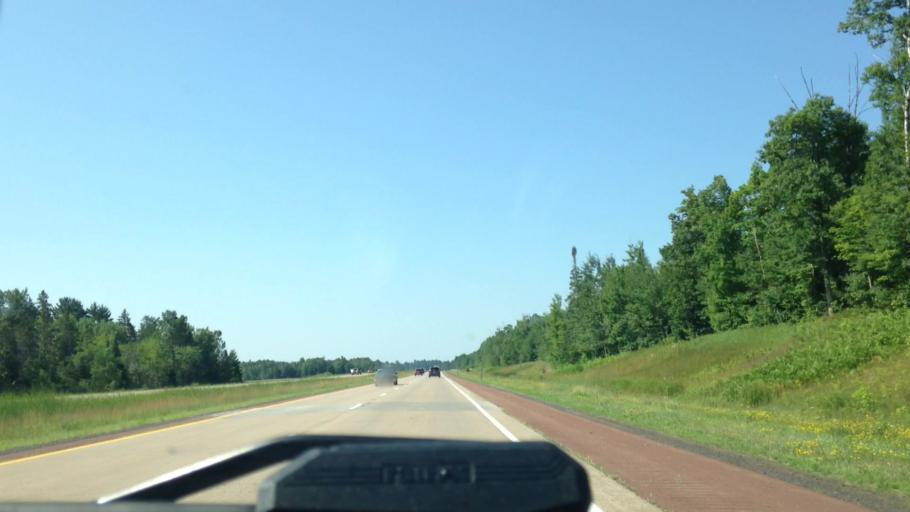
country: US
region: Wisconsin
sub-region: Douglas County
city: Lake Nebagamon
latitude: 46.3707
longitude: -91.8278
